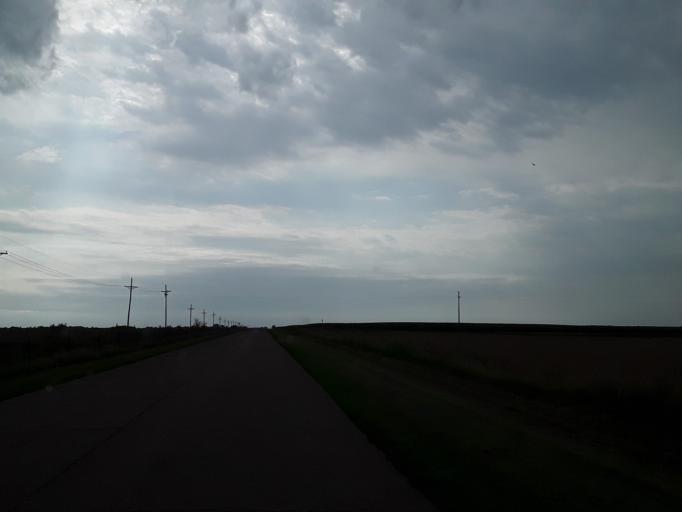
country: US
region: Nebraska
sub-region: Saunders County
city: Yutan
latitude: 41.1613
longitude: -96.4424
